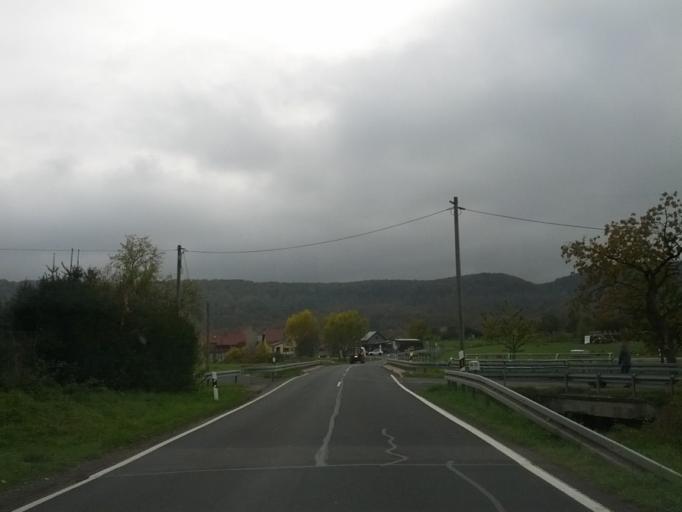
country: DE
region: Thuringia
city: Frankenroda
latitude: 51.1204
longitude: 10.2663
